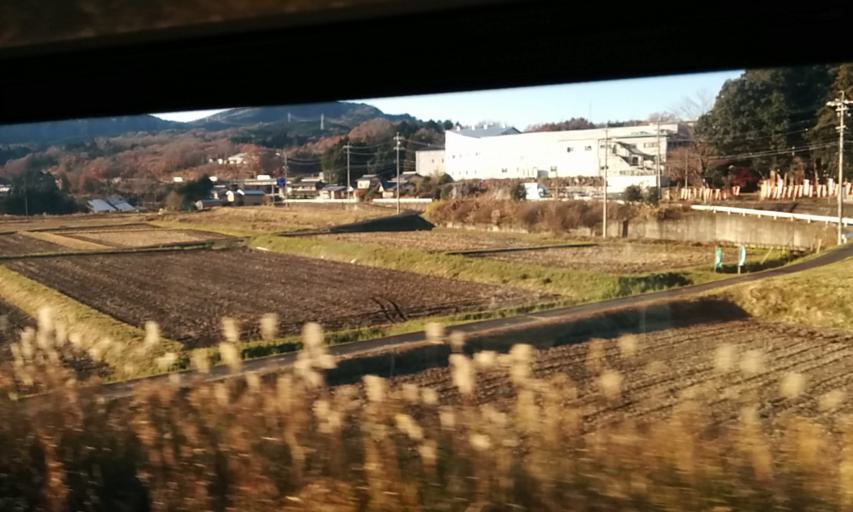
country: JP
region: Gifu
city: Mizunami
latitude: 35.4320
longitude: 137.3451
